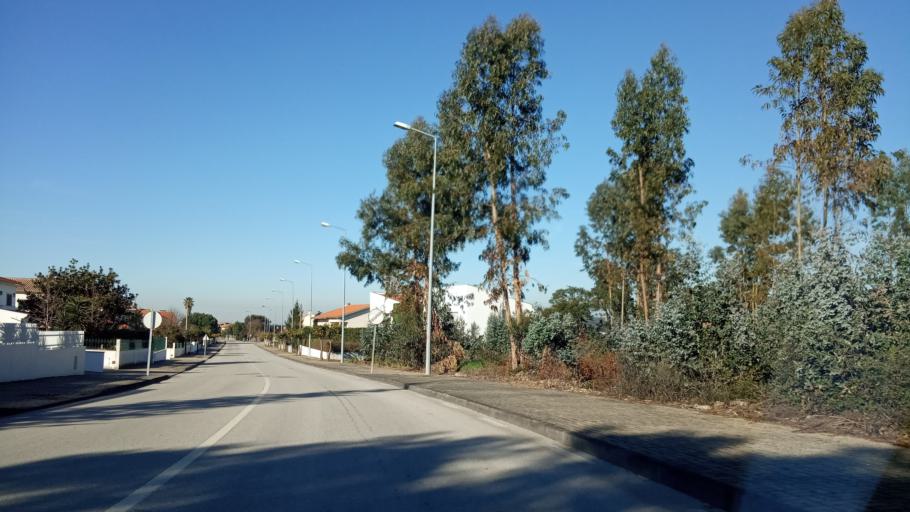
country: PT
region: Aveiro
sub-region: Anadia
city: Anadia
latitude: 40.4290
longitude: -8.4244
